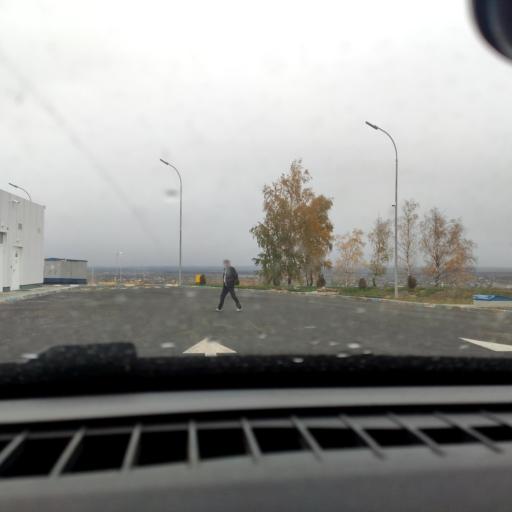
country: RU
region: Belgorod
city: Alekseyevka
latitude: 50.6443
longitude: 38.6778
